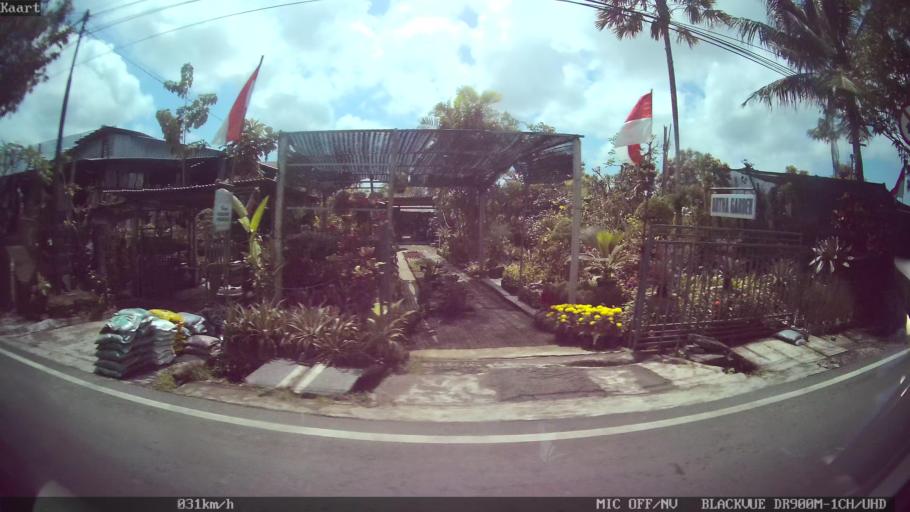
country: ID
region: Bali
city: Banjar Sedang
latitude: -8.5647
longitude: 115.2803
